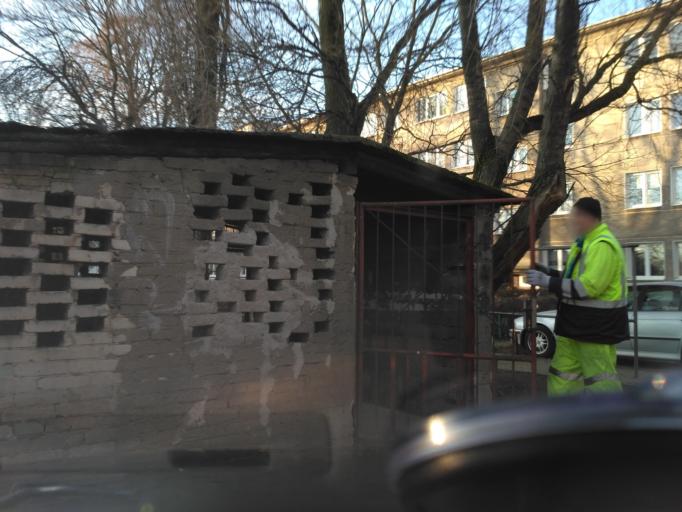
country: PL
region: Lublin Voivodeship
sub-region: Powiat lubelski
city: Lublin
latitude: 51.2613
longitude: 22.5691
